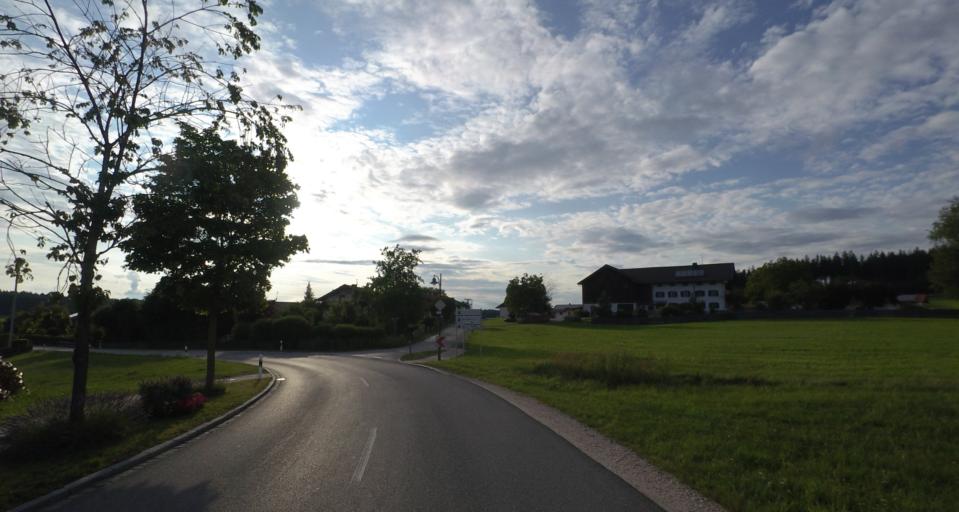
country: DE
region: Bavaria
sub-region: Upper Bavaria
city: Nussdorf
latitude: 47.9083
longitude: 12.5931
